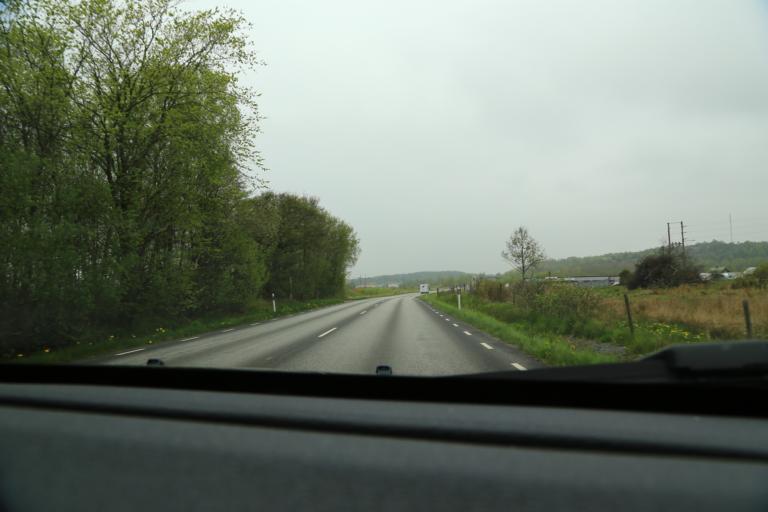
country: SE
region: Halland
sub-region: Varbergs Kommun
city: Varberg
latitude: 57.1649
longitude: 12.2366
